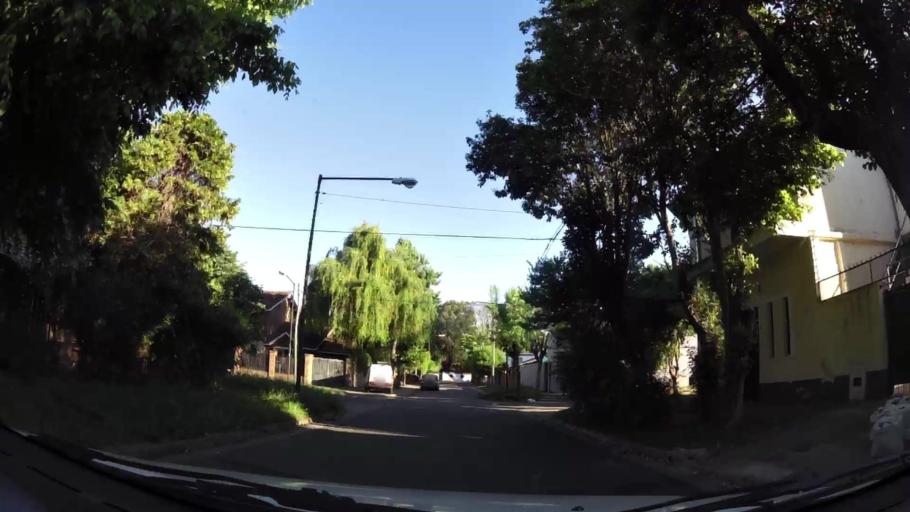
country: AR
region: Buenos Aires
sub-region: Partido de San Isidro
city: San Isidro
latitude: -34.4751
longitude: -58.5527
